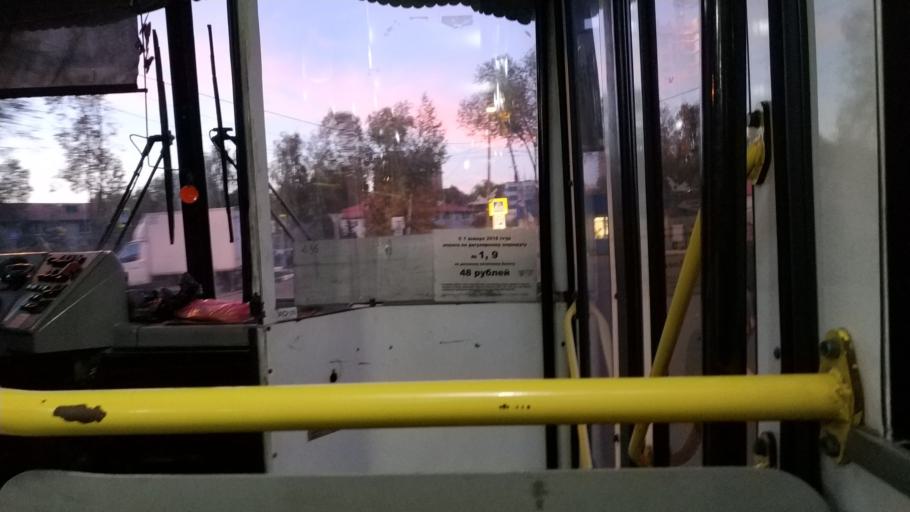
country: RU
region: Moskovskaya
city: Lobnya
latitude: 56.0234
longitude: 37.4209
